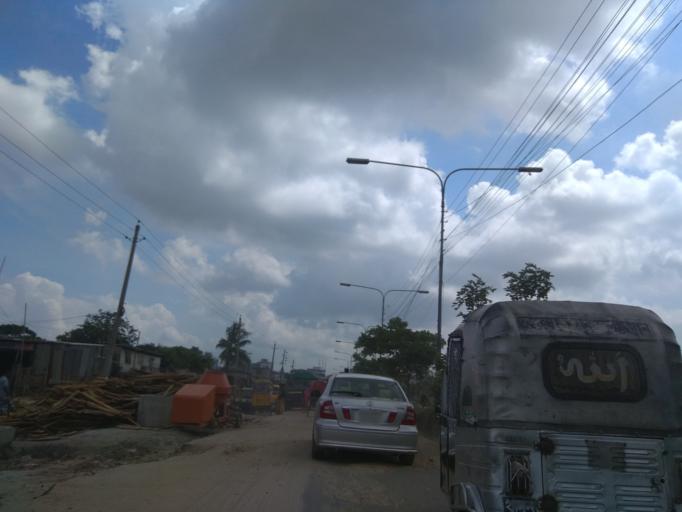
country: BD
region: Dhaka
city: Paltan
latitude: 23.8096
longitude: 90.3912
